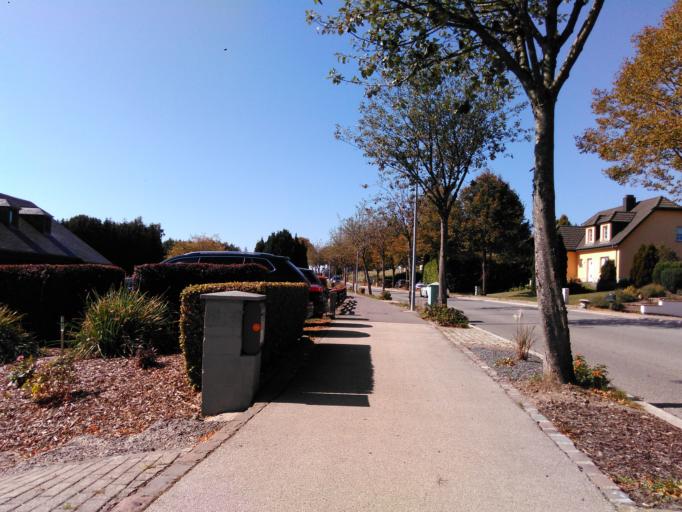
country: LU
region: Diekirch
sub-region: Canton de Redange
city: Rambrouch
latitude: 49.8397
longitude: 5.8341
